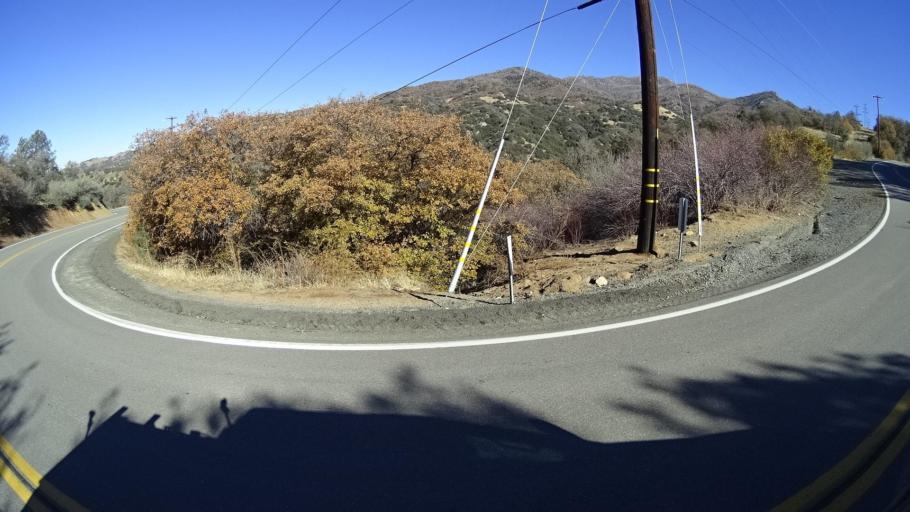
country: US
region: California
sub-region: Kern County
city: Alta Sierra
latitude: 35.7380
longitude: -118.6333
